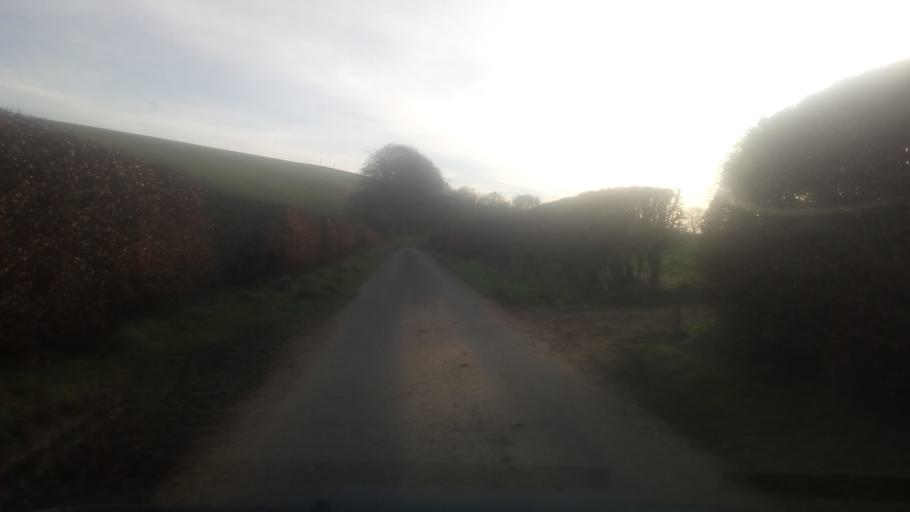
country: GB
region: Scotland
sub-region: The Scottish Borders
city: Jedburgh
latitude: 55.4677
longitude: -2.6286
